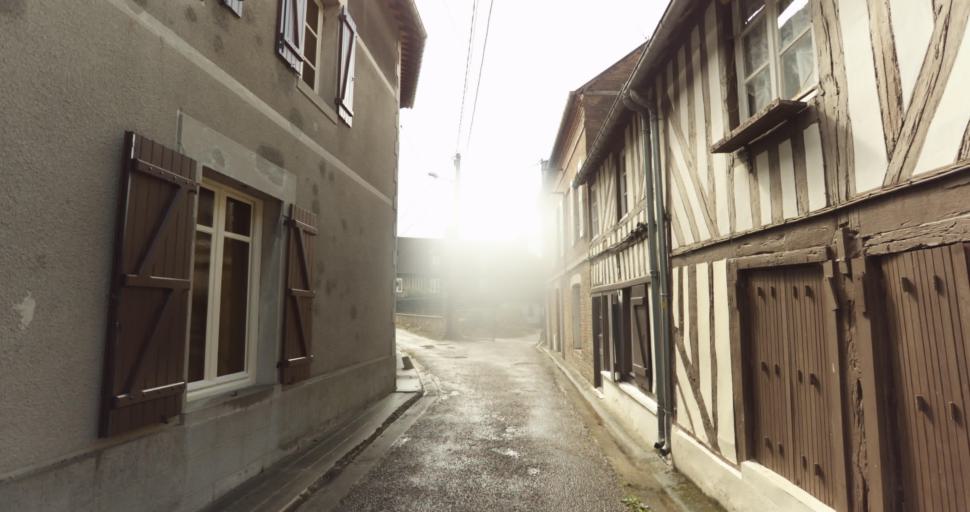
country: FR
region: Lower Normandy
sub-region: Departement de l'Orne
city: Vimoutiers
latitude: 48.9252
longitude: 0.2004
